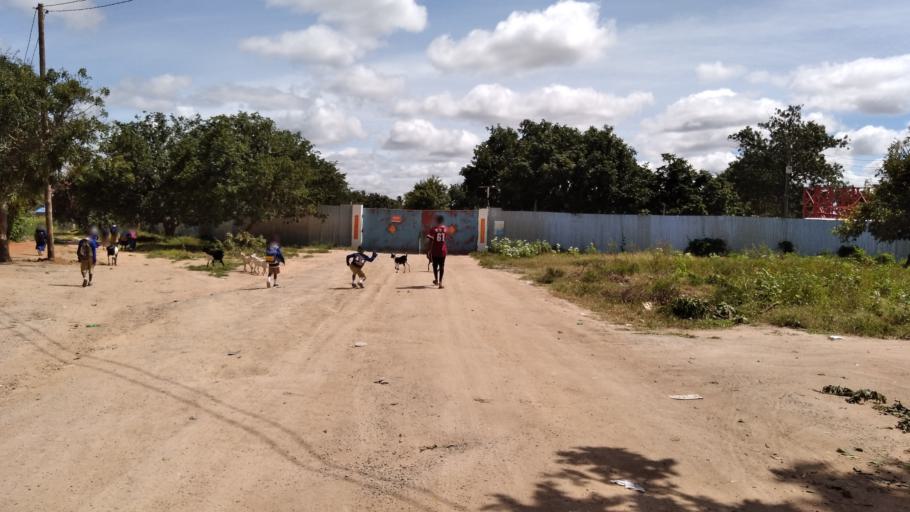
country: TZ
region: Dodoma
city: Dodoma
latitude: -6.1573
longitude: 35.7417
